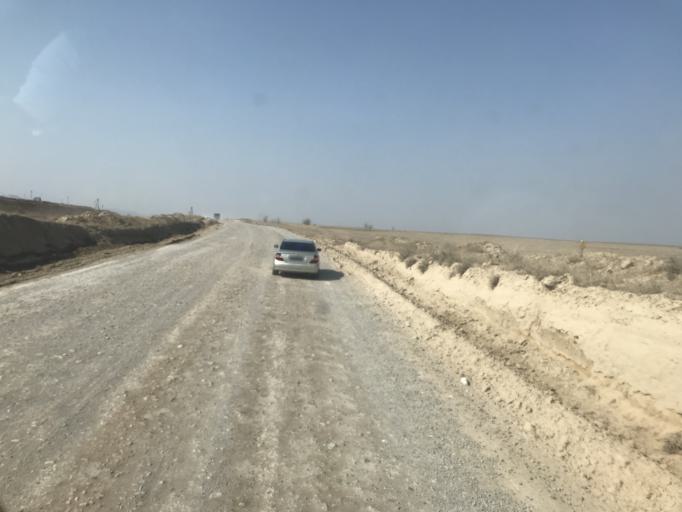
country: KG
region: Chuy
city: Bystrovka
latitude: 43.3224
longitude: 76.0517
